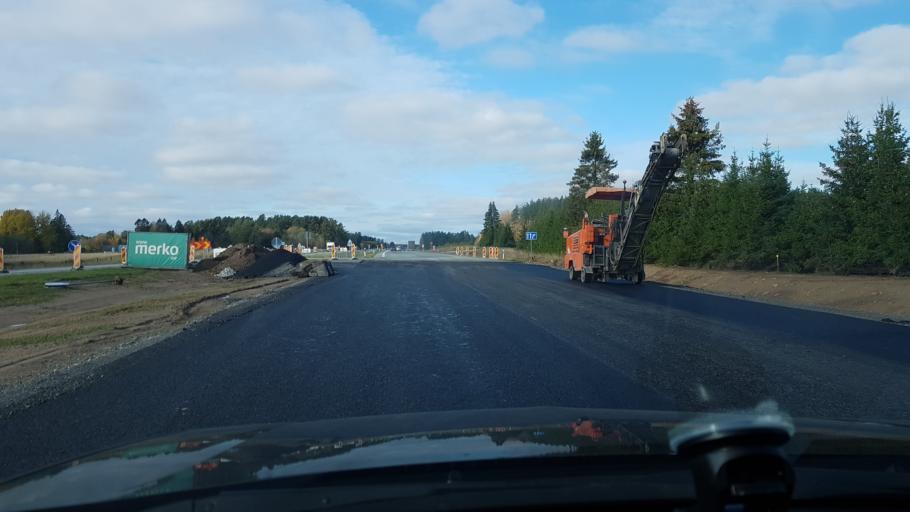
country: EE
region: Laeaene-Virumaa
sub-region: Kadrina vald
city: Kadrina
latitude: 59.4447
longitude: 26.0951
